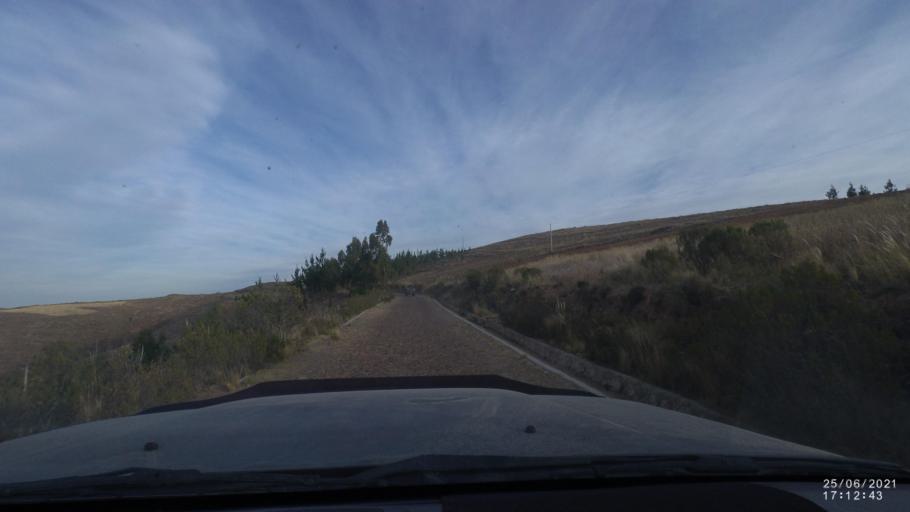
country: BO
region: Cochabamba
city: Arani
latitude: -17.8532
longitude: -65.7004
